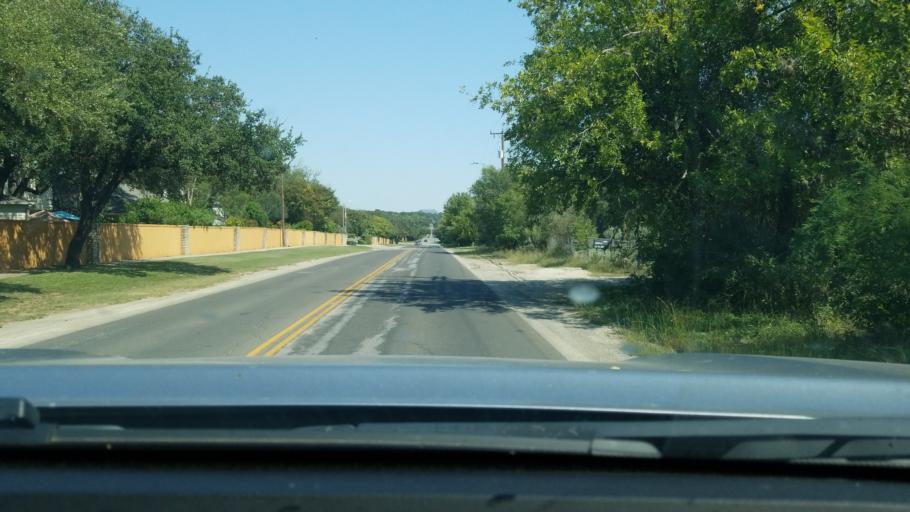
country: US
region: Texas
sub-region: Bexar County
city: Leon Valley
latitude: 29.5447
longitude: -98.6114
